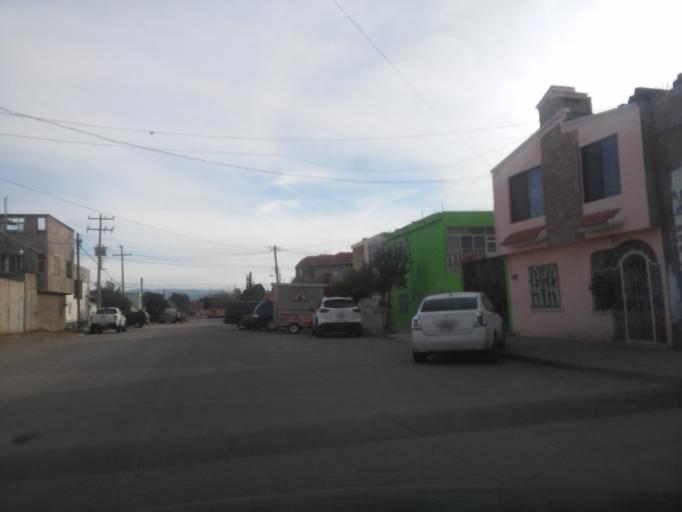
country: MX
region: Durango
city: Victoria de Durango
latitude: 24.0200
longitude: -104.6349
